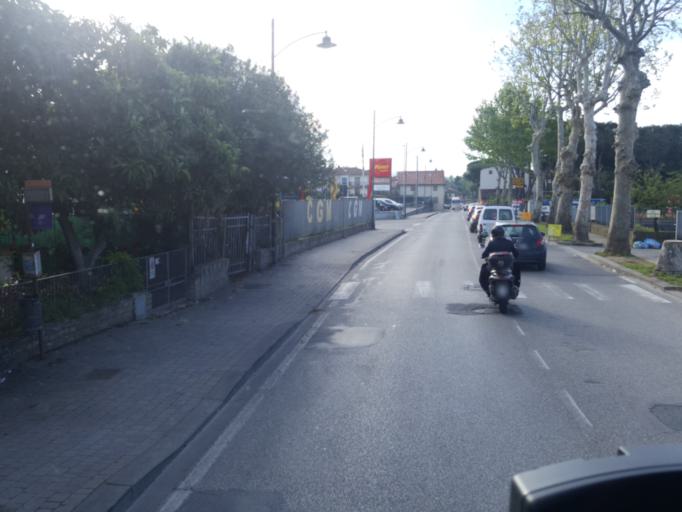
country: IT
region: Tuscany
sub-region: Province of Florence
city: Calenzano
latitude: 43.8472
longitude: 11.1752
